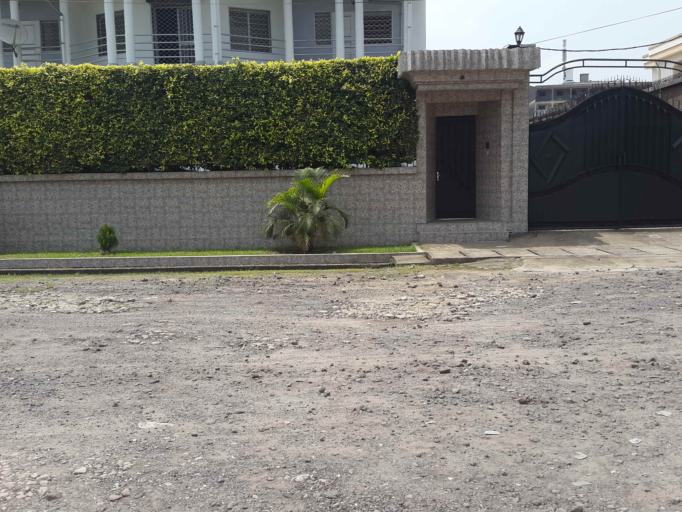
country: CM
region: Littoral
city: Douala
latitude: 4.0881
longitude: 9.7346
